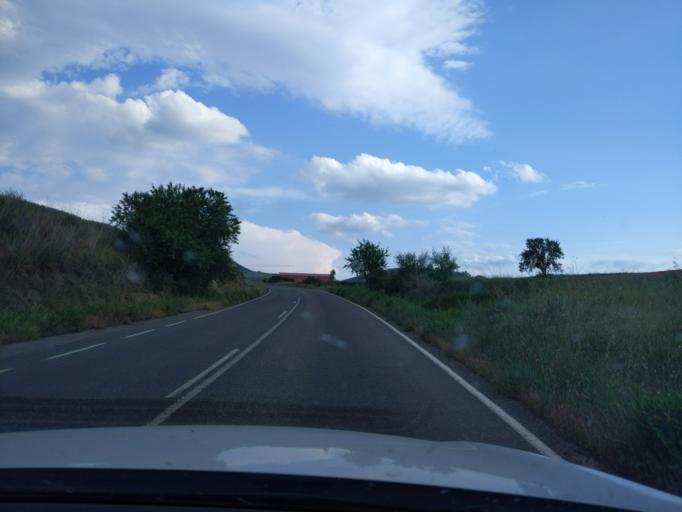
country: ES
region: La Rioja
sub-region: Provincia de La Rioja
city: Alberite
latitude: 42.3836
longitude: -2.4242
